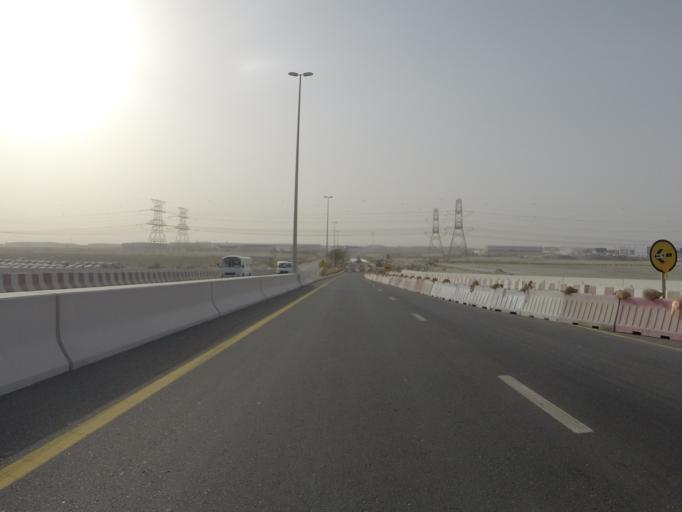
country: AE
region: Dubai
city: Dubai
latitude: 24.9571
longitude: 55.1022
